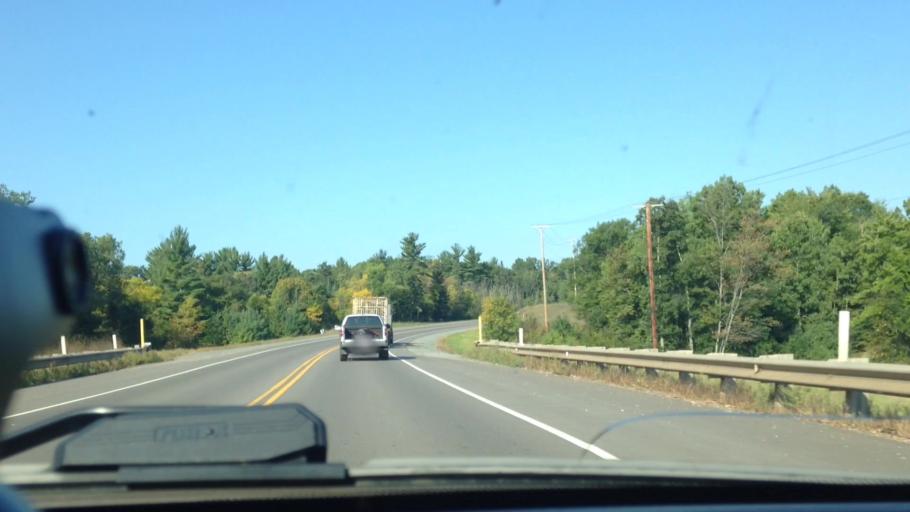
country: US
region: Michigan
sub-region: Dickinson County
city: Iron Mountain
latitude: 45.8662
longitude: -88.0754
